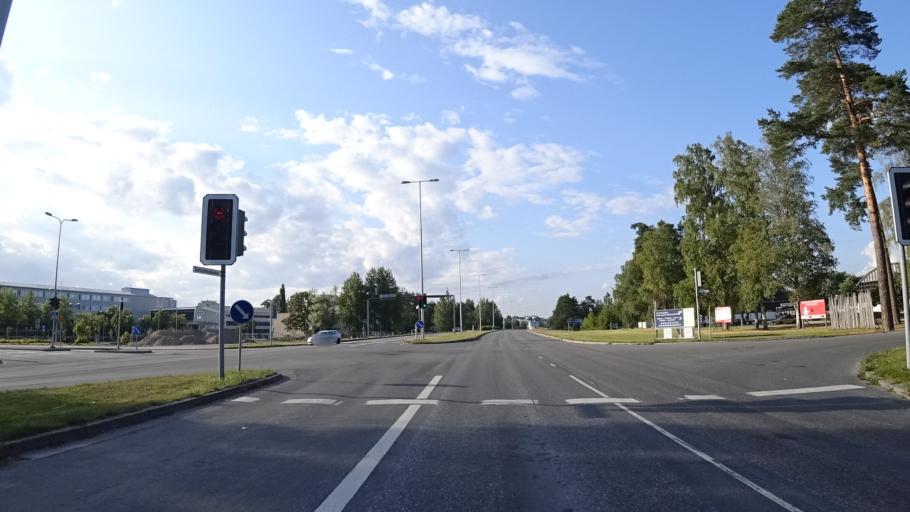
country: FI
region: South Karelia
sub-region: Imatra
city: Imatra
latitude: 61.1844
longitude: 28.7792
